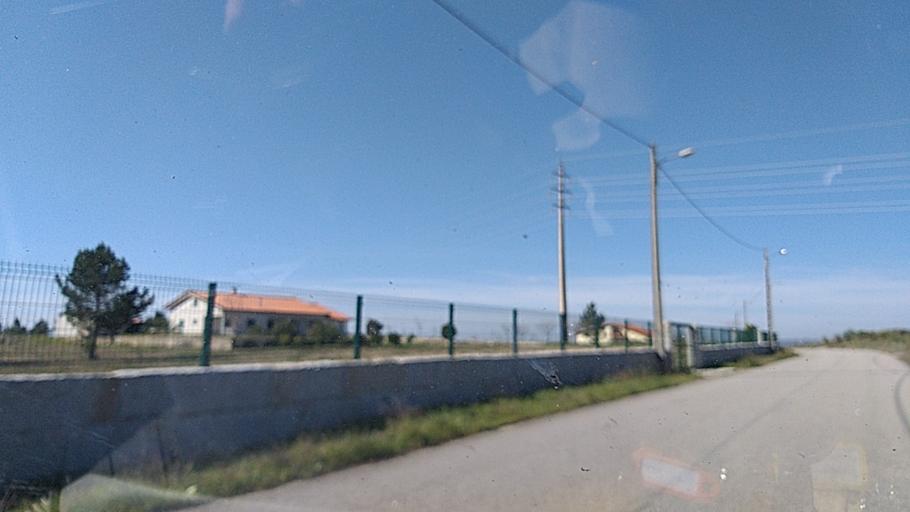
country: PT
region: Guarda
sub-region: Celorico da Beira
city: Celorico da Beira
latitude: 40.5925
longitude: -7.4432
